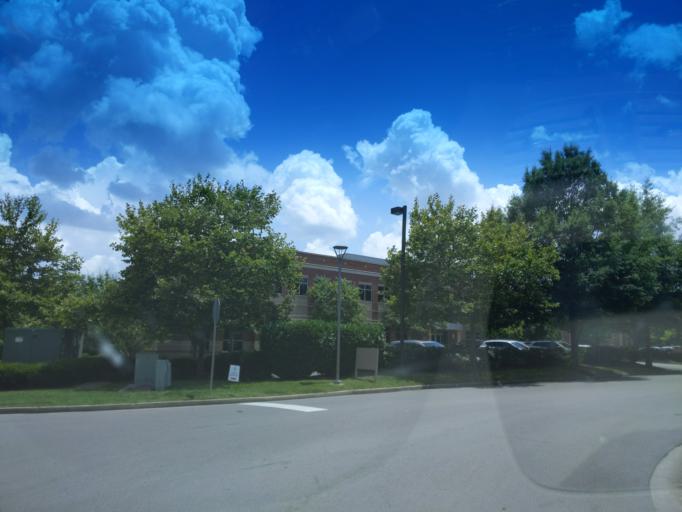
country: US
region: Tennessee
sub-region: Williamson County
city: Brentwood
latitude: 36.0419
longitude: -86.7682
